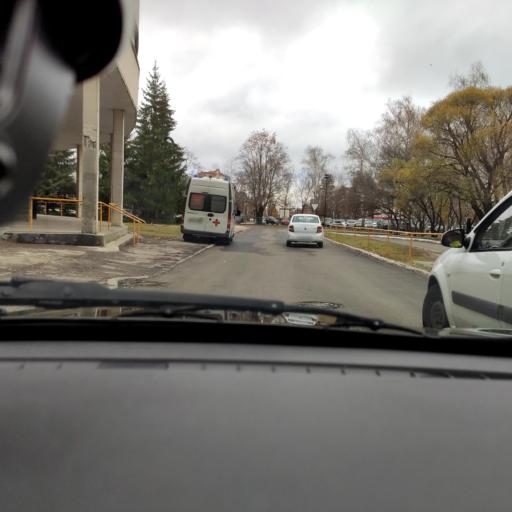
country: RU
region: Samara
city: Tol'yatti
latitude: 53.5225
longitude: 49.3255
